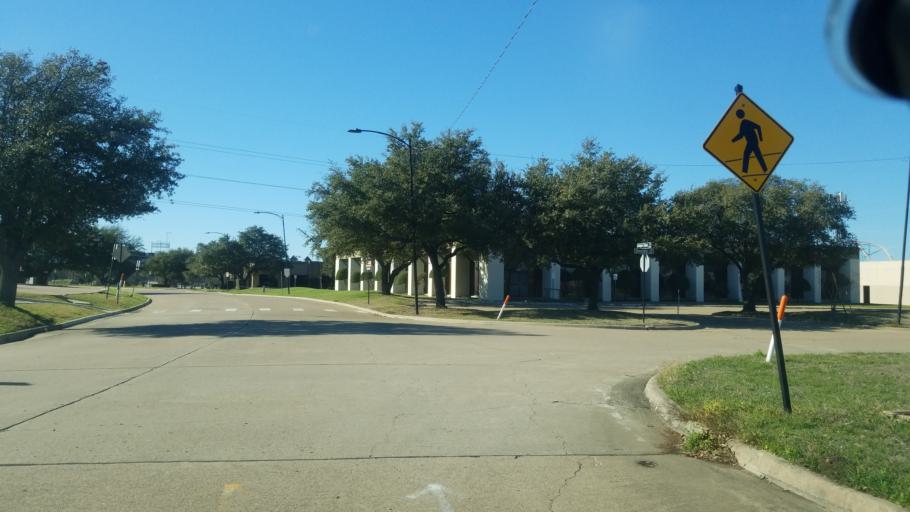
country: US
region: Texas
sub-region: Tarrant County
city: Arlington
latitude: 32.7505
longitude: -97.0722
